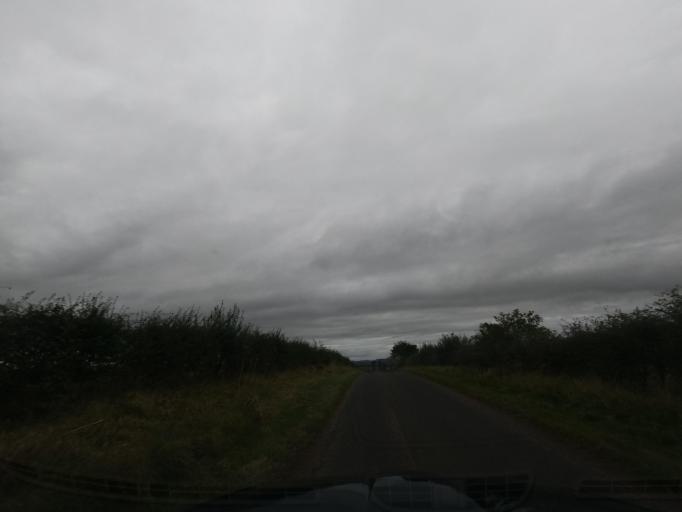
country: GB
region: England
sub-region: Northumberland
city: Ford
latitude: 55.7063
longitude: -2.0872
